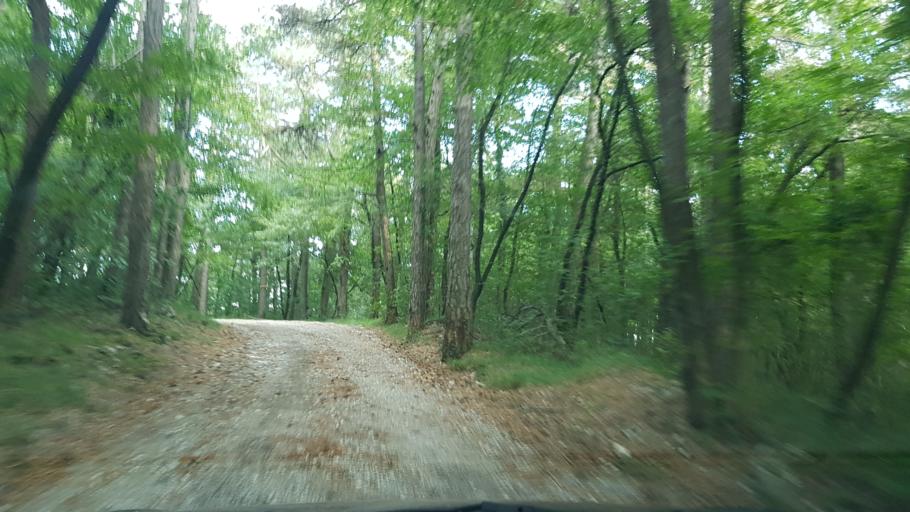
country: SI
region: Nova Gorica
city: Prvacina
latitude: 45.8555
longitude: 13.7002
